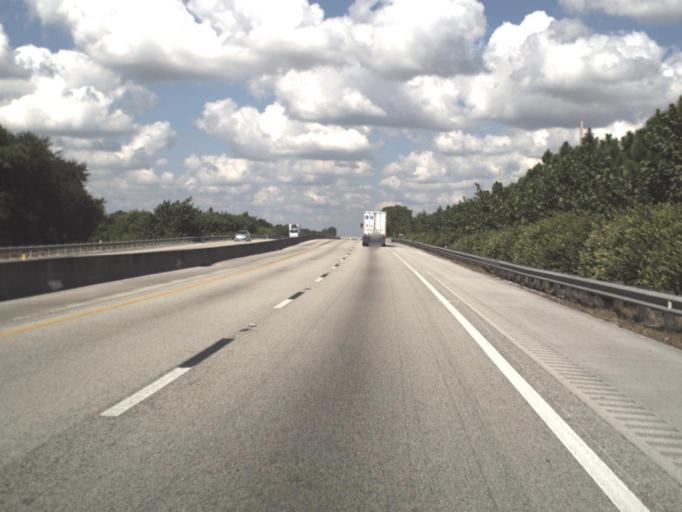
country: US
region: Florida
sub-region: Saint Lucie County
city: Port Saint Lucie
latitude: 27.2604
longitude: -80.3510
